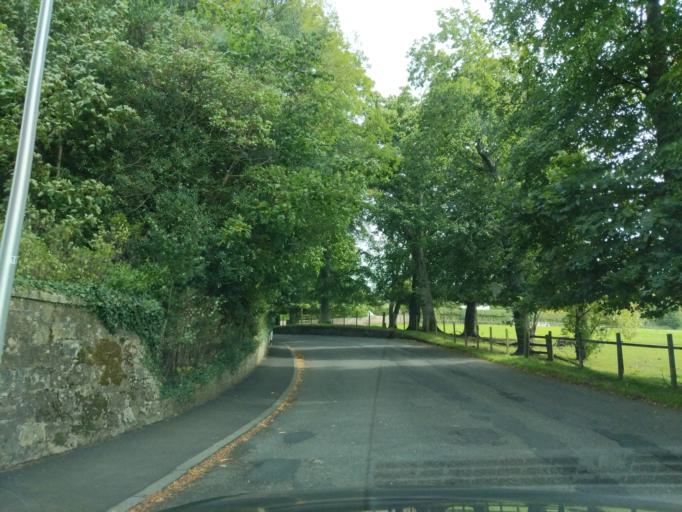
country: GB
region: Scotland
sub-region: The Scottish Borders
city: Melrose
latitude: 55.5988
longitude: -2.7375
